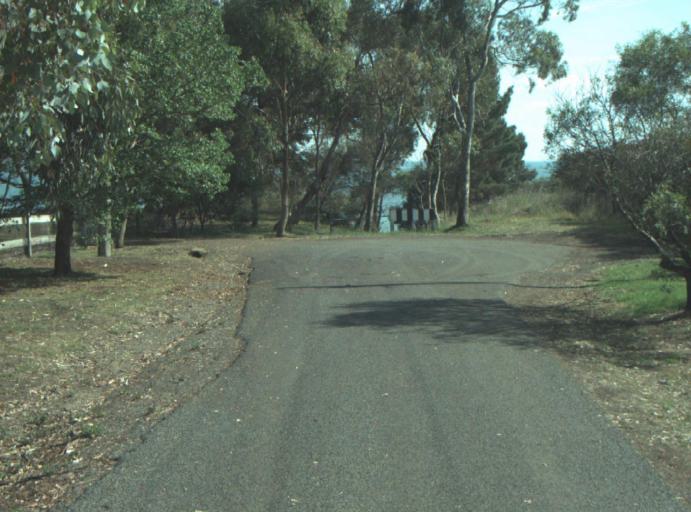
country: AU
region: Victoria
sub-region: Greater Geelong
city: Clifton Springs
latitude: -38.1618
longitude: 144.5168
